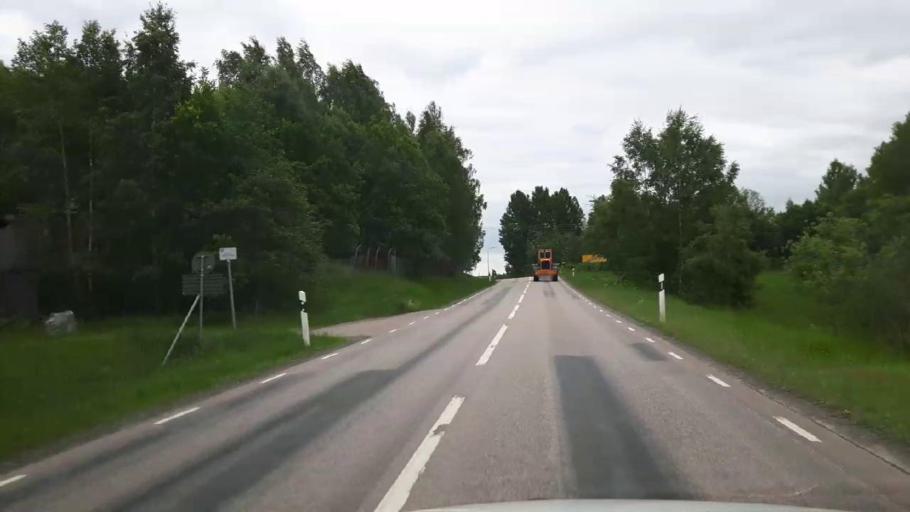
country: SE
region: Vaestmanland
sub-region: Kopings Kommun
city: Kolsva
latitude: 59.6102
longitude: 15.8282
